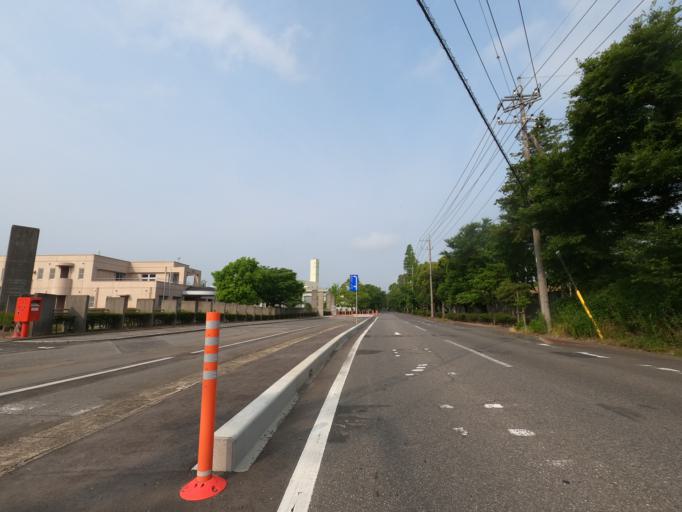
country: JP
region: Ibaraki
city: Moriya
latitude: 35.9534
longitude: 139.9500
